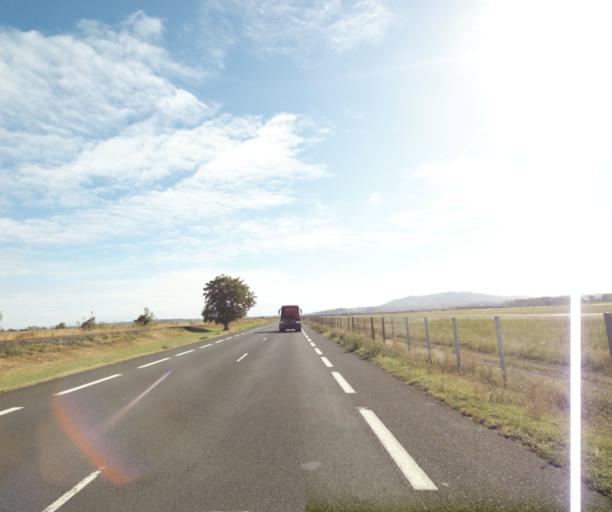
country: FR
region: Auvergne
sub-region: Departement du Puy-de-Dome
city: Aulnat
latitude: 45.7910
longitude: 3.1815
